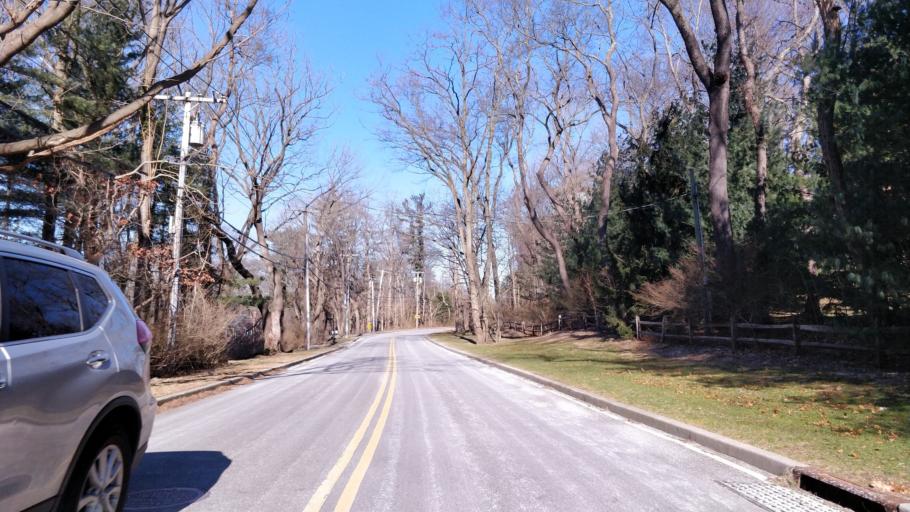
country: US
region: New York
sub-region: Nassau County
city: Brookville
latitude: 40.8103
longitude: -73.5782
